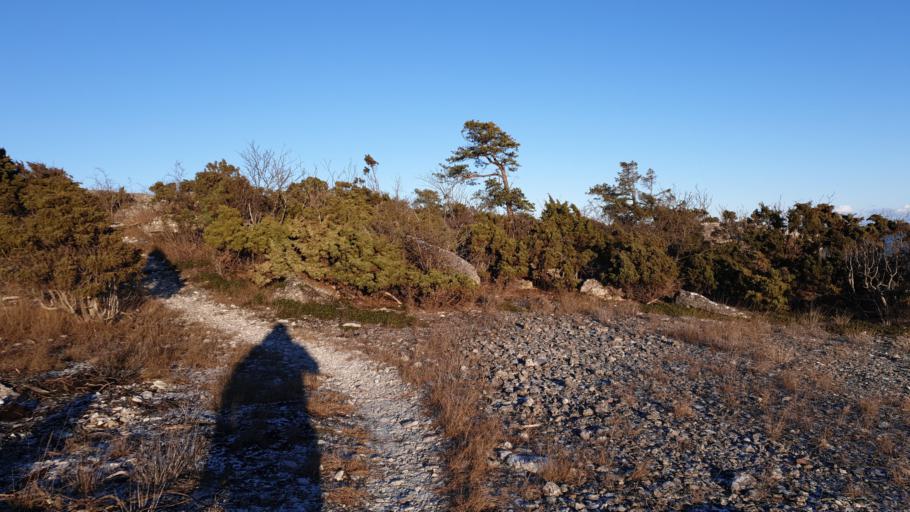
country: SE
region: Gotland
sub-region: Gotland
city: Slite
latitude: 57.3729
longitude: 18.8110
